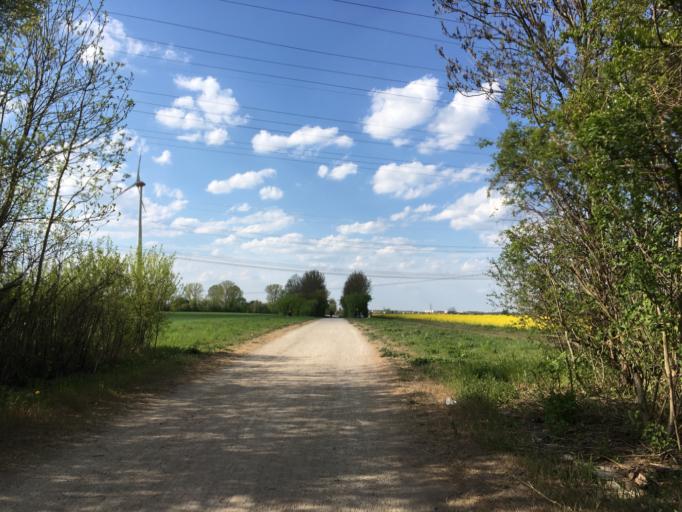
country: DE
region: Berlin
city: Wartenberg
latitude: 52.5927
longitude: 13.5077
